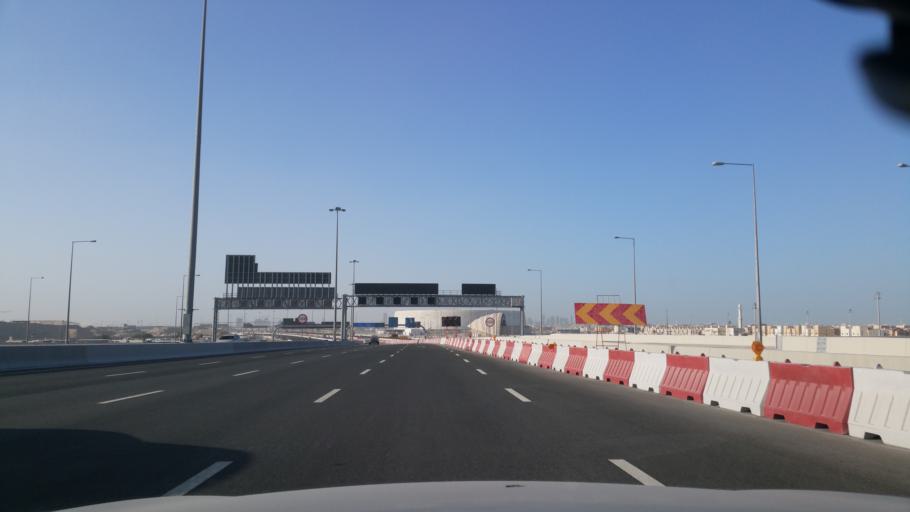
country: QA
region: Baladiyat ad Dawhah
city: Doha
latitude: 25.2229
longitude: 51.5340
